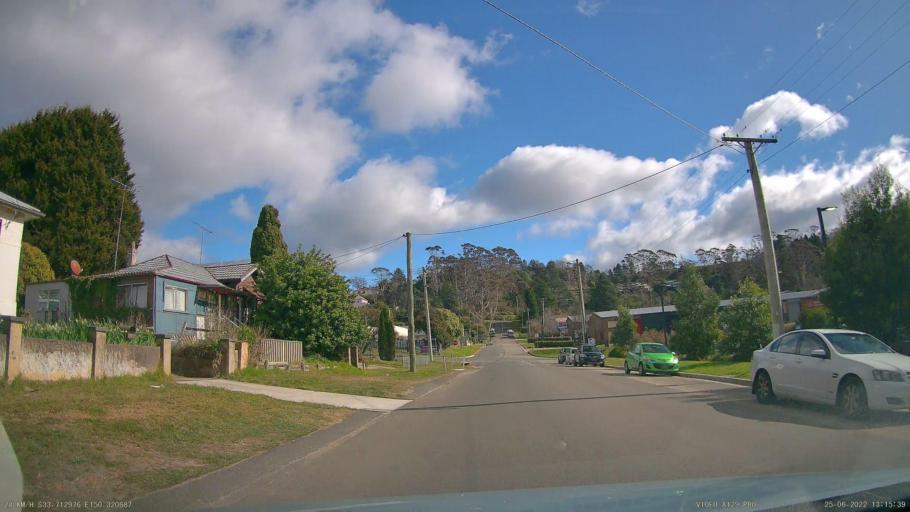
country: AU
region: New South Wales
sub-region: Blue Mountains Municipality
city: Leura
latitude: -33.7130
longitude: 150.3205
